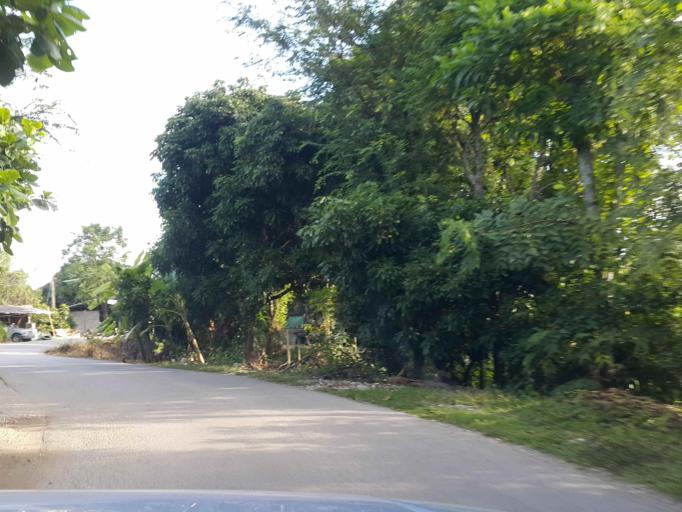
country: TH
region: Chiang Mai
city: San Sai
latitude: 18.9070
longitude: 98.9789
